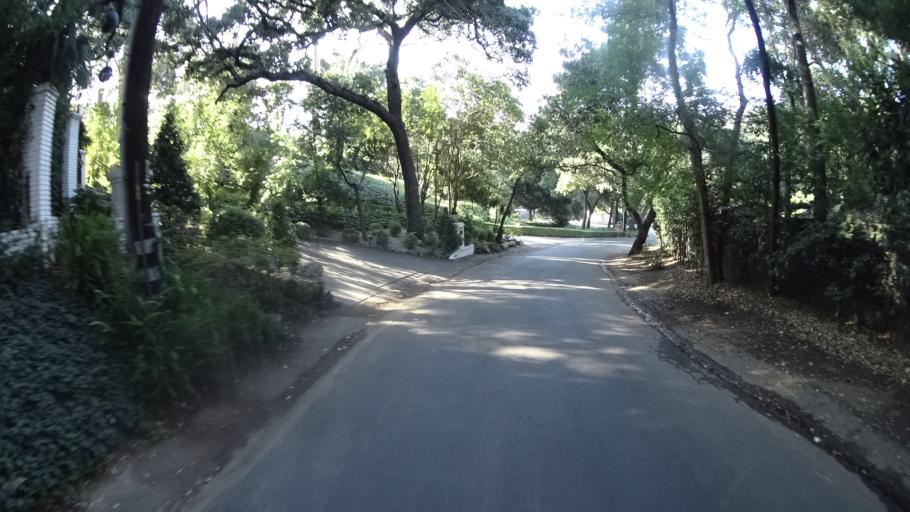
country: US
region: California
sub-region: Los Angeles County
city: Universal City
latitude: 34.1296
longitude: -118.3903
